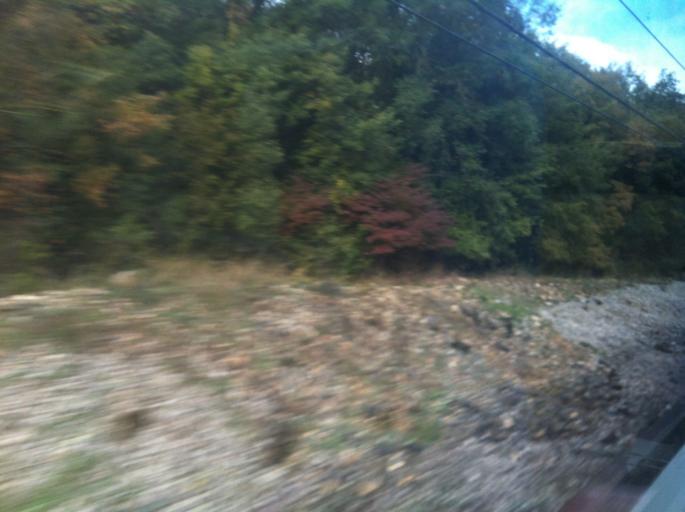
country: ES
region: Basque Country
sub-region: Provincia de Alava
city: Arminon
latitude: 42.7818
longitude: -2.8268
